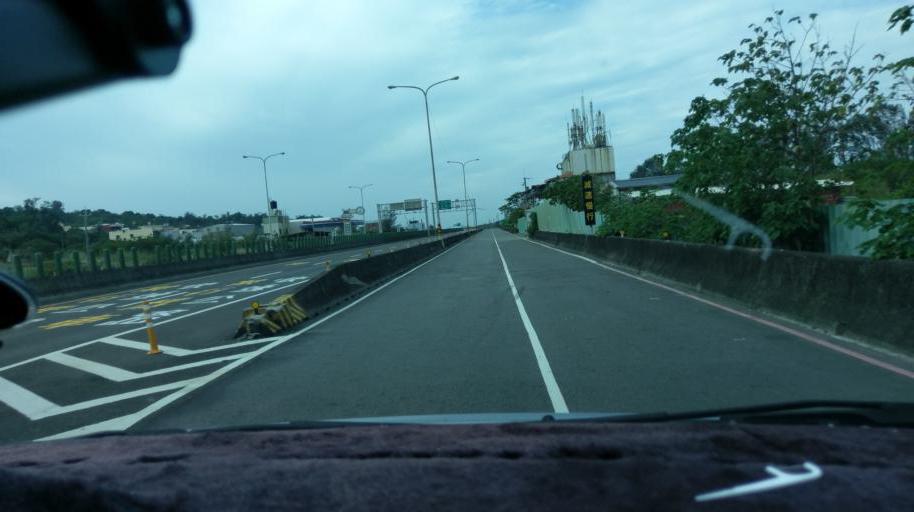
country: TW
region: Taiwan
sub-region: Hsinchu
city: Hsinchu
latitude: 24.7349
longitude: 120.8830
